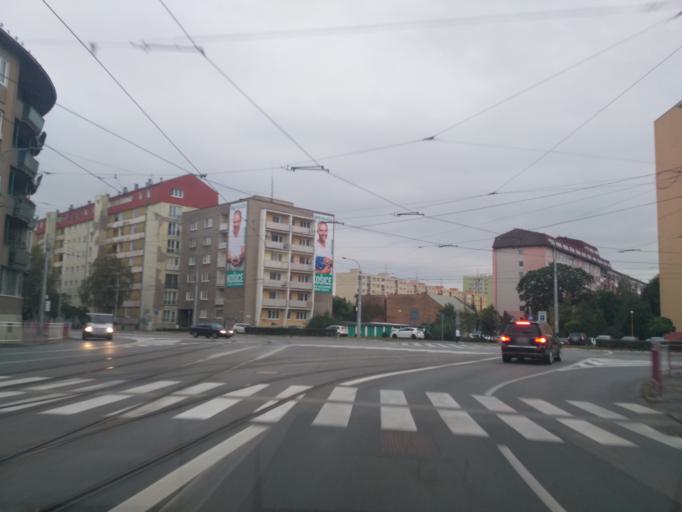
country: SK
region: Kosicky
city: Kosice
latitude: 48.7273
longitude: 21.2471
